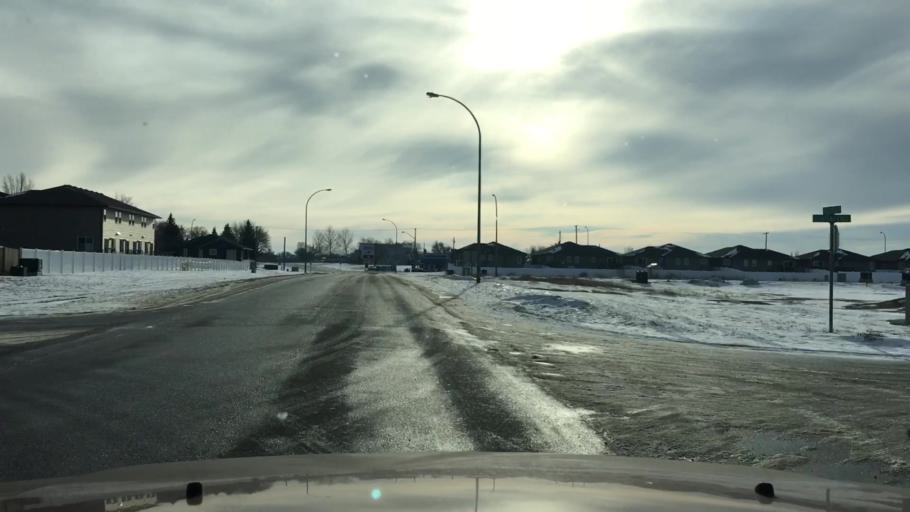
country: CA
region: Saskatchewan
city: Pilot Butte
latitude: 50.4860
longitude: -104.4202
